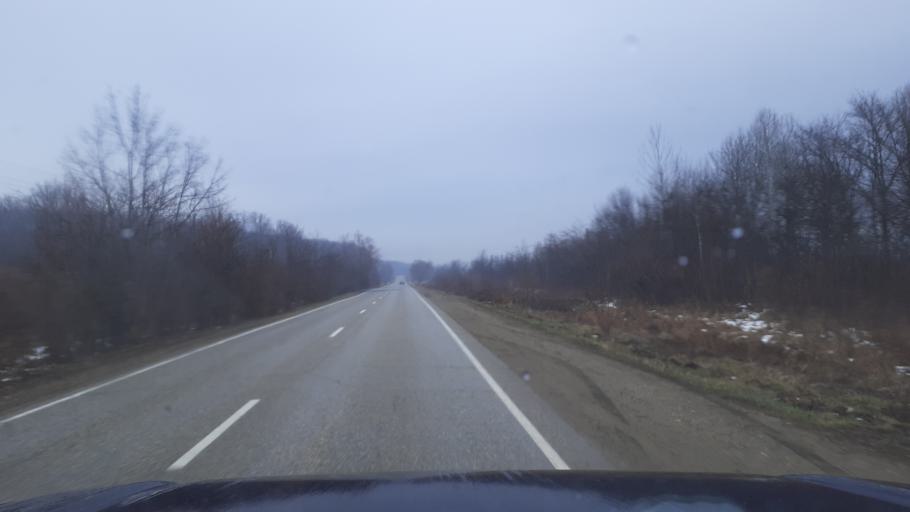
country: RU
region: Krasnodarskiy
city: Neftegorsk
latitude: 44.2623
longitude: 39.7764
